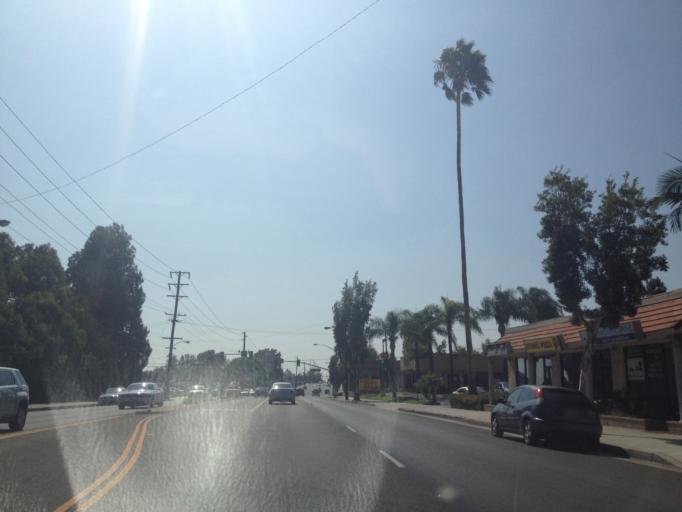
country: US
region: California
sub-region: Orange County
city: La Habra
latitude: 33.9391
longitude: -117.9578
